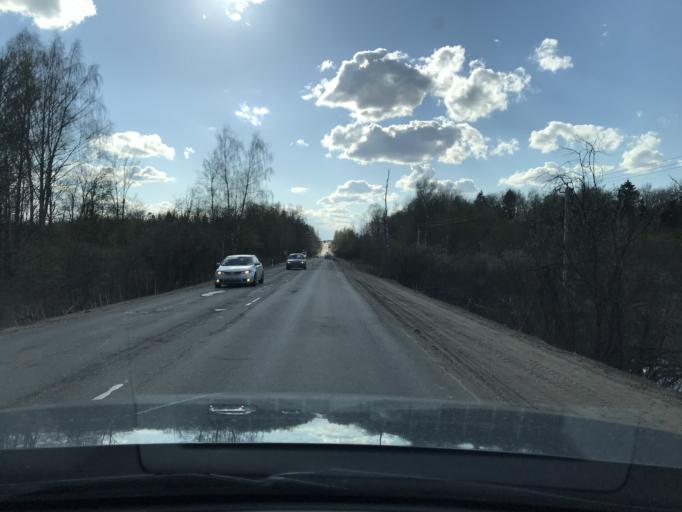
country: RU
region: Vladimir
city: Strunino
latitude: 56.4176
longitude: 38.5711
